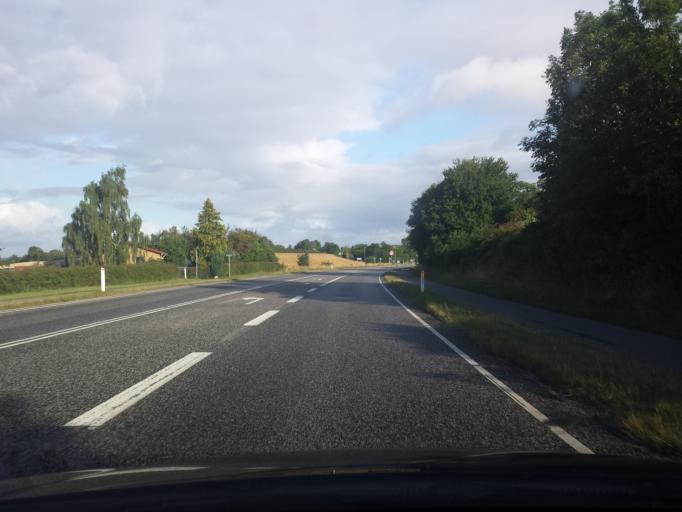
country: DK
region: South Denmark
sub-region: Sonderborg Kommune
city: Guderup
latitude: 54.9863
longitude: 9.8653
